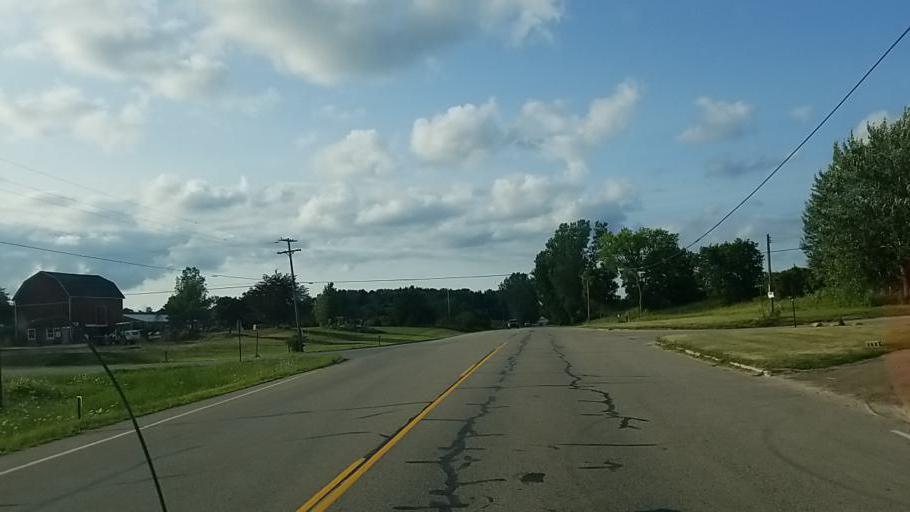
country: US
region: Michigan
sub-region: Kent County
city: Lowell
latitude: 43.0289
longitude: -85.3520
